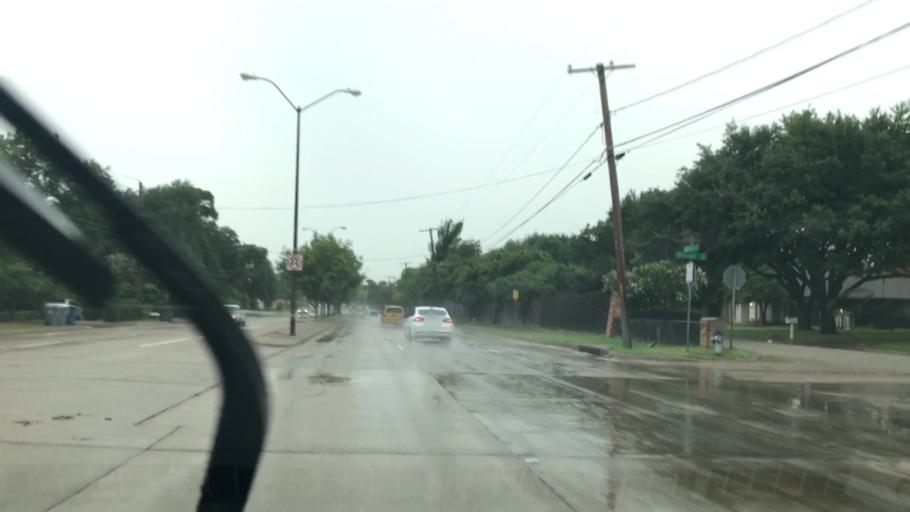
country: US
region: Texas
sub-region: Dallas County
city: Addison
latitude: 32.9400
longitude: -96.7902
